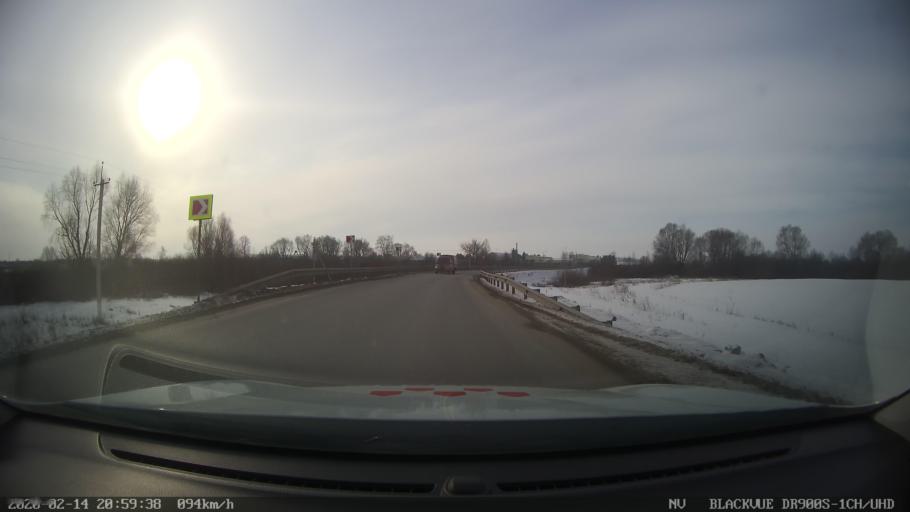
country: RU
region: Tatarstan
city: Kuybyshevskiy Zaton
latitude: 55.1768
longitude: 49.2354
